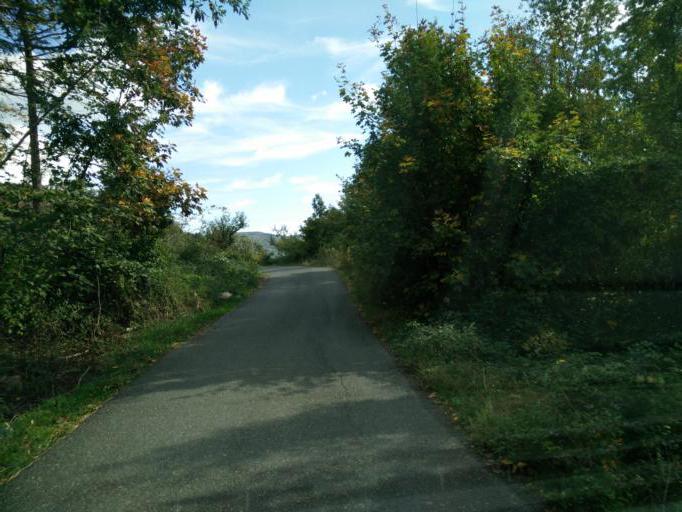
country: IT
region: Tuscany
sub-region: Provincia di Massa-Carrara
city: Patigno
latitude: 44.3540
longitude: 9.7516
